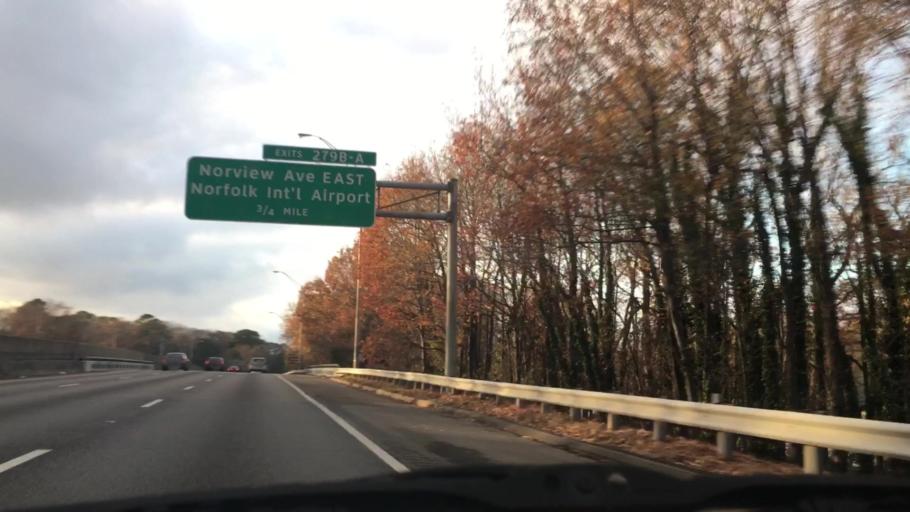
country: US
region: Virginia
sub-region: City of Norfolk
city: Norfolk
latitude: 36.8845
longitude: -76.2225
